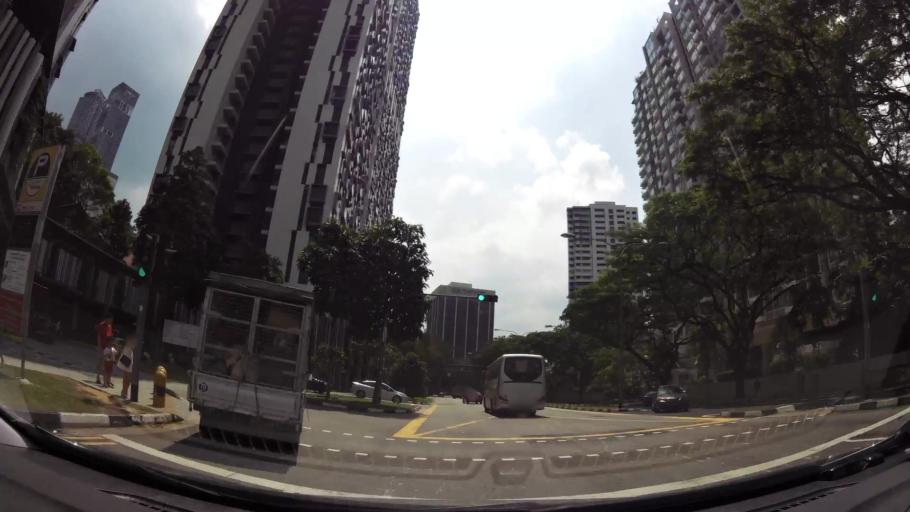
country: SG
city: Singapore
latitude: 1.2765
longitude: 103.8409
